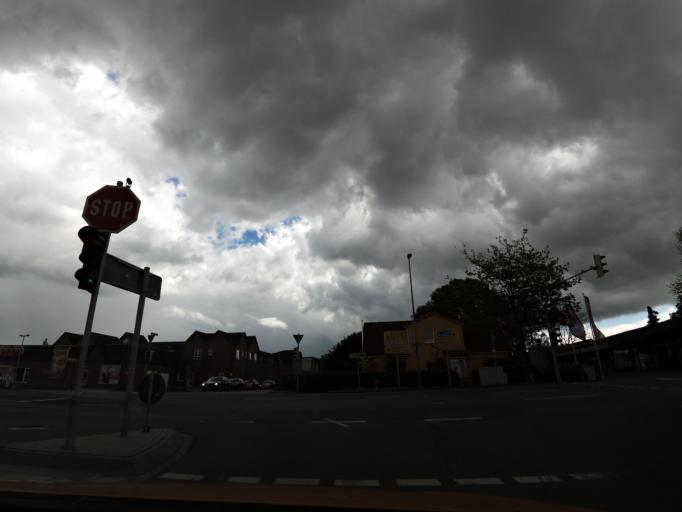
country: DE
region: Lower Saxony
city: Ganderkesee
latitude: 53.0947
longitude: 8.5306
